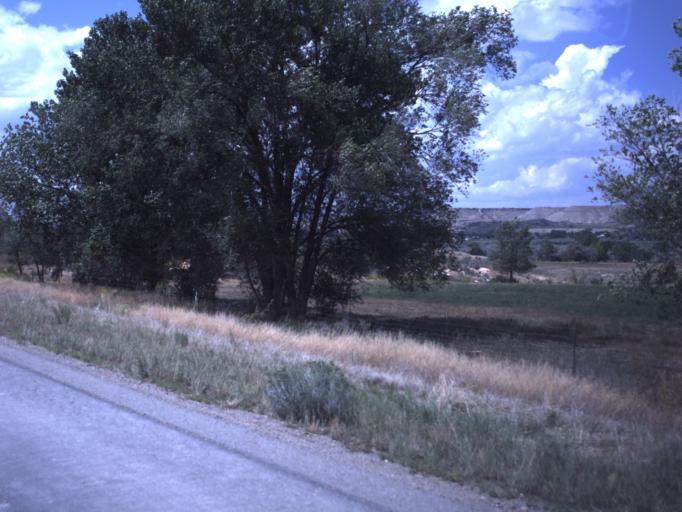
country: US
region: Utah
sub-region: Duchesne County
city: Duchesne
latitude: 40.1693
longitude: -110.3098
